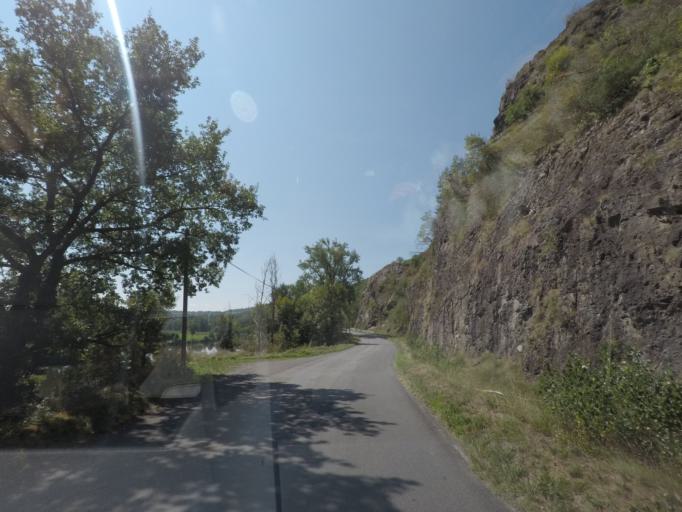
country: FR
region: Midi-Pyrenees
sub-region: Departement de l'Aveyron
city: Livinhac-le-Haut
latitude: 44.6104
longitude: 2.2335
